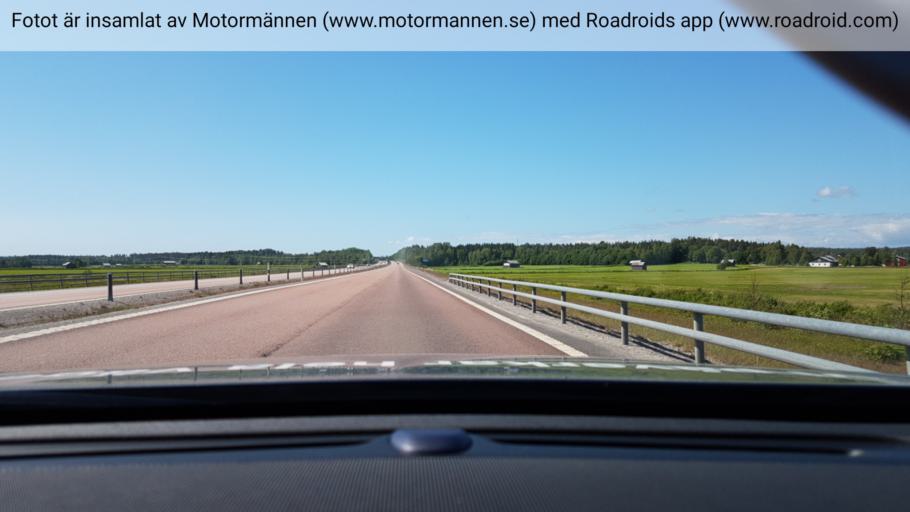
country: SE
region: Vaesterbotten
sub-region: Umea Kommun
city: Umea
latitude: 63.8010
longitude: 20.2352
